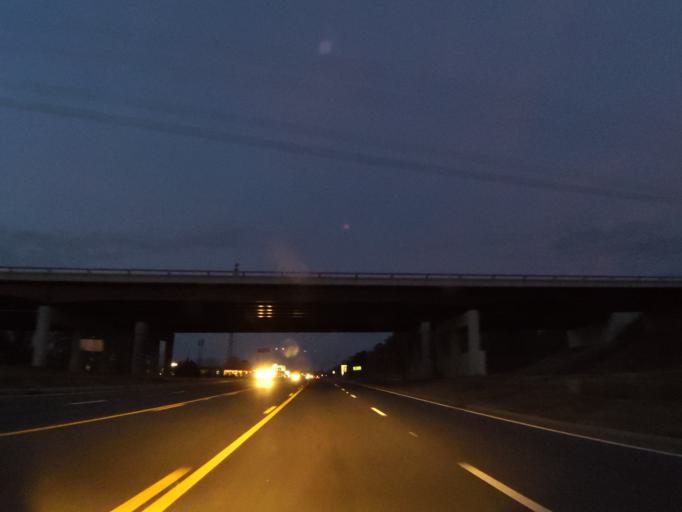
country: US
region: Tennessee
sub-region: Polk County
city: Benton
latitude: 35.1264
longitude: -84.7175
